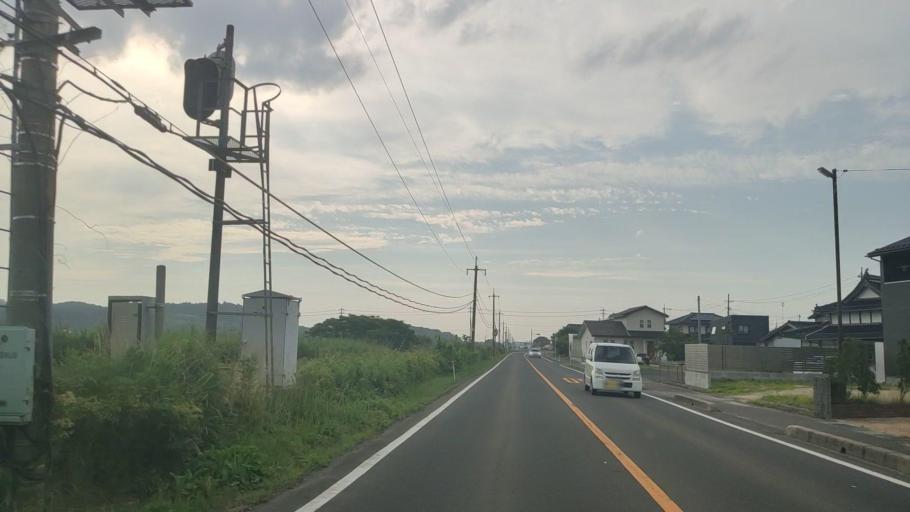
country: JP
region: Tottori
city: Kurayoshi
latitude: 35.4748
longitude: 133.8225
